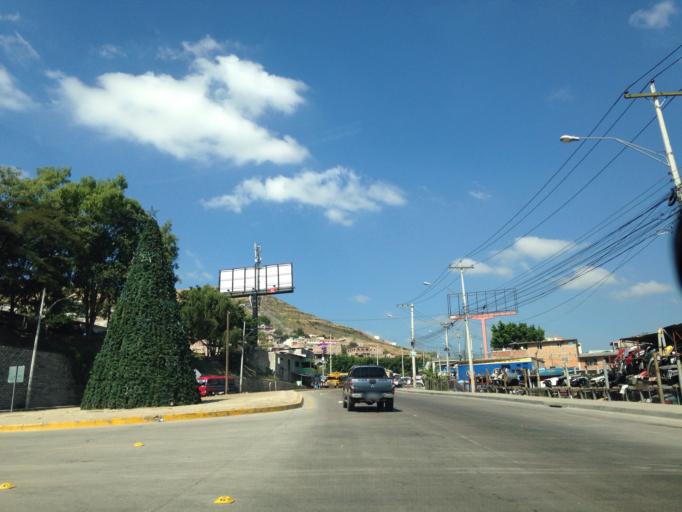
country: HN
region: Francisco Morazan
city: El Lolo
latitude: 14.1053
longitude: -87.2433
